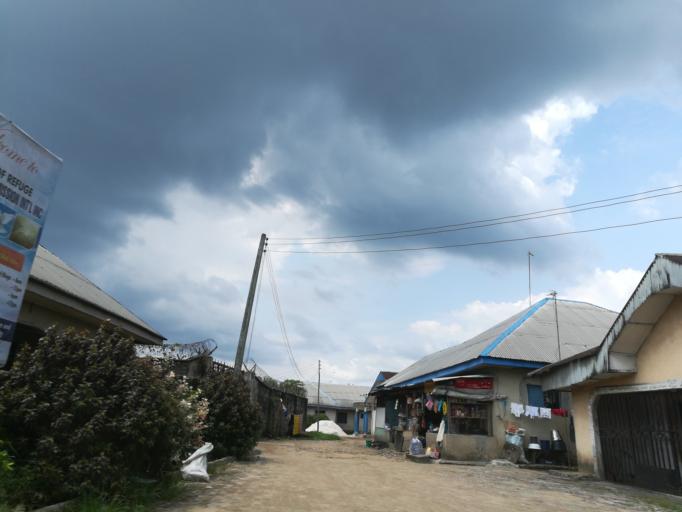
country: NG
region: Rivers
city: Okrika
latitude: 4.7316
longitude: 7.1529
